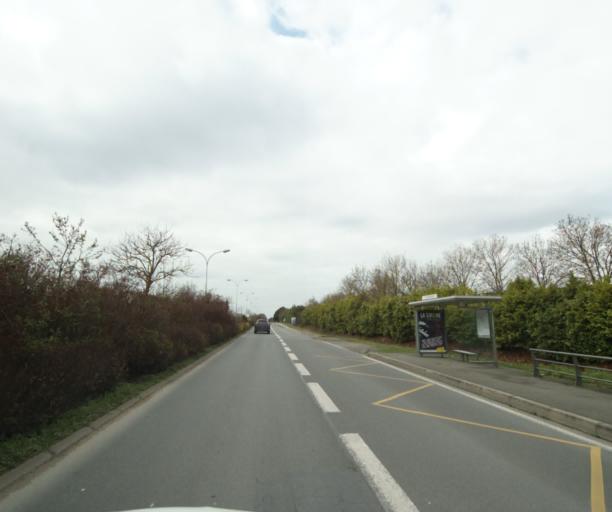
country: FR
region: Poitou-Charentes
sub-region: Departement de la Charente-Maritime
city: Lagord
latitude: 46.1899
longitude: -1.1475
